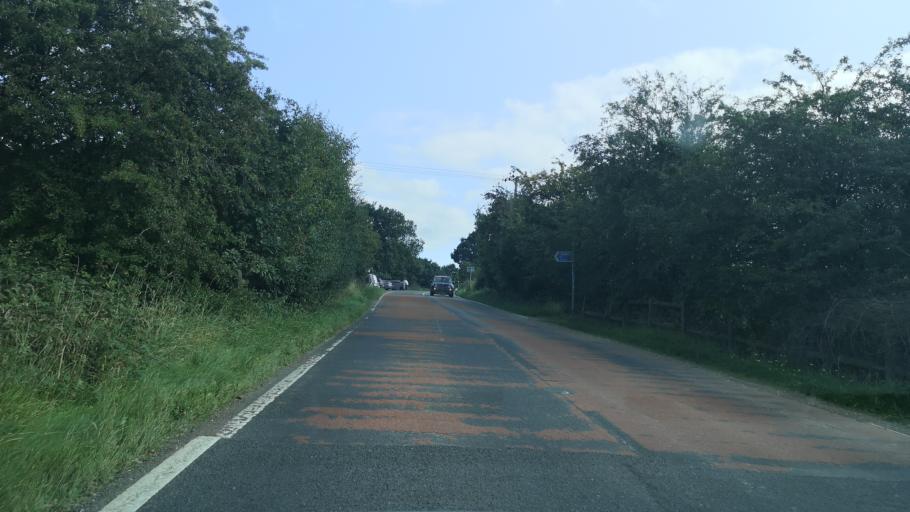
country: GB
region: England
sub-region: Barnsley
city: Royston
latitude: 53.6234
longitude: -1.4493
